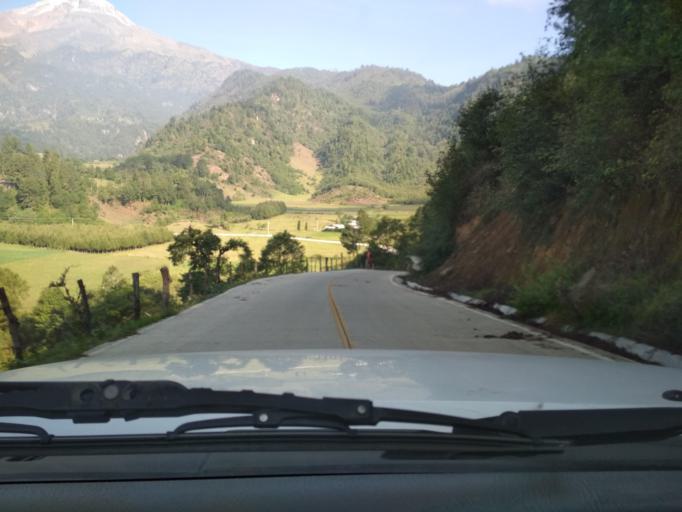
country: MX
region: Veracruz
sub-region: La Perla
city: Chilapa
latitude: 19.0035
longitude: -97.1786
